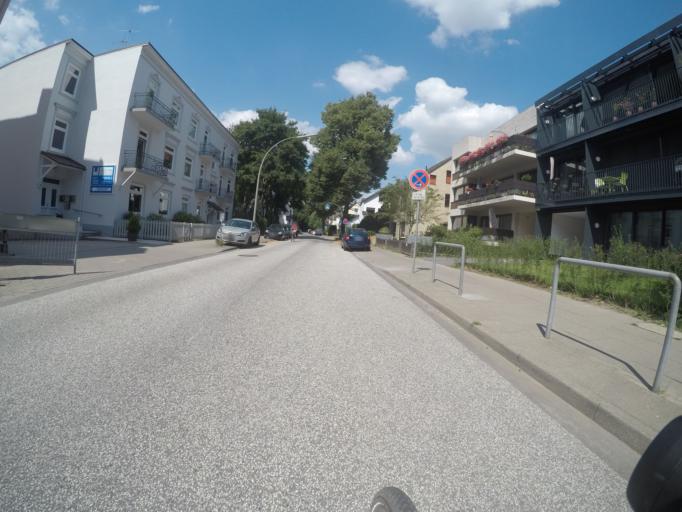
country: DE
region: Hamburg
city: Bergedorf
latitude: 53.4945
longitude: 10.2147
